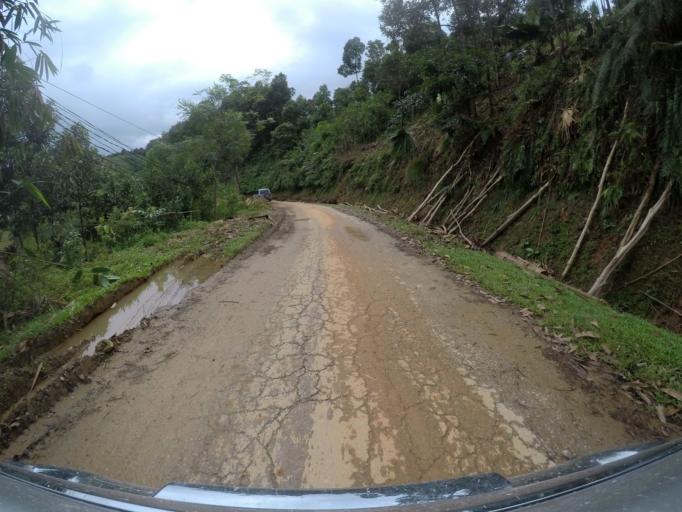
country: VN
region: Yen Bai
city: Co Phuc
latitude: 21.8222
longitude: 104.6234
